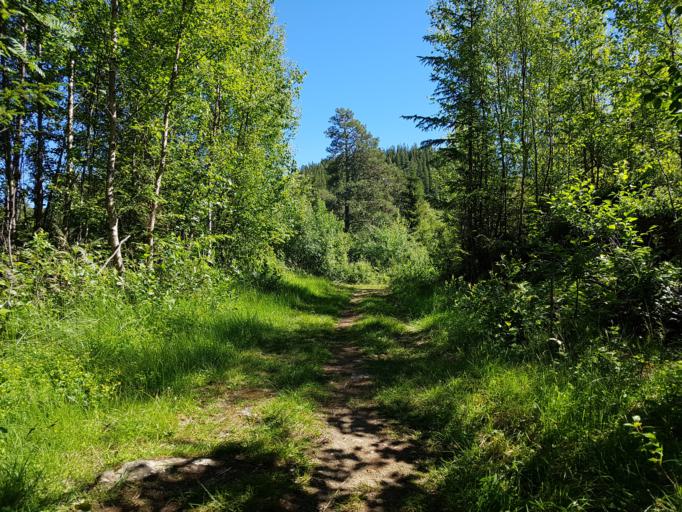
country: NO
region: Sor-Trondelag
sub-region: Melhus
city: Melhus
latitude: 63.4357
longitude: 10.2083
